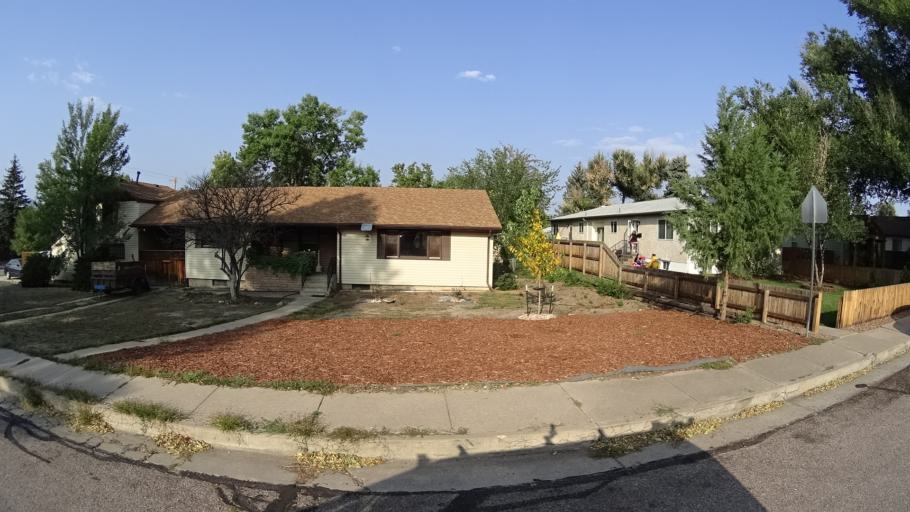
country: US
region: Colorado
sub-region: El Paso County
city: Colorado Springs
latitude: 38.8467
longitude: -104.7915
